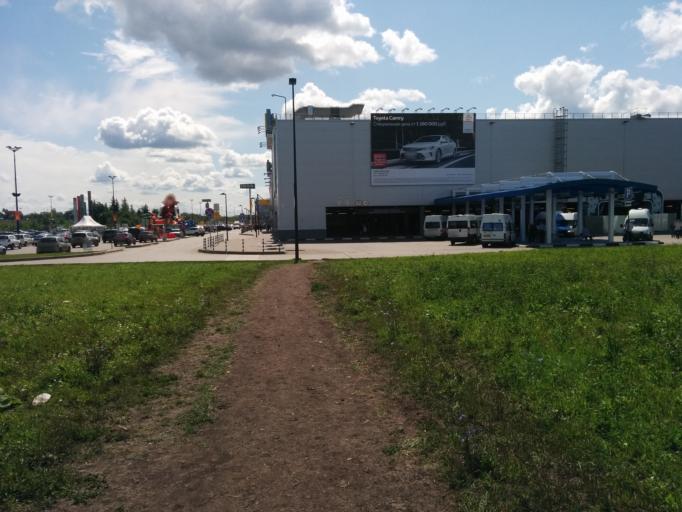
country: RU
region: Bashkortostan
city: Ufa
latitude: 54.6772
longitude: 55.9309
